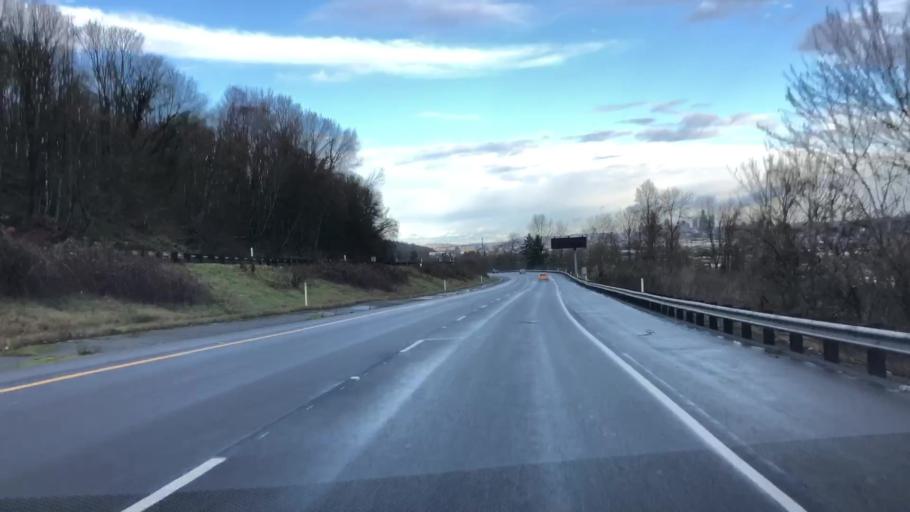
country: US
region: Washington
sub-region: King County
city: White Center
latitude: 47.5173
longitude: -122.3300
